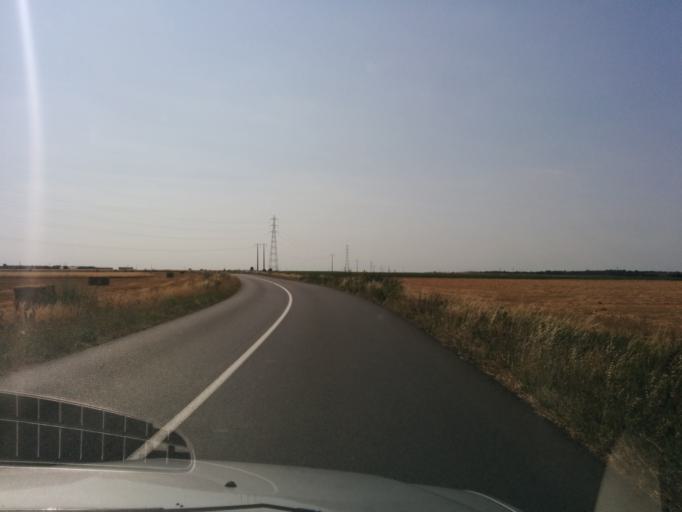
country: FR
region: Poitou-Charentes
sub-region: Departement des Deux-Sevres
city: Airvault
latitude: 46.8152
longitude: -0.0834
